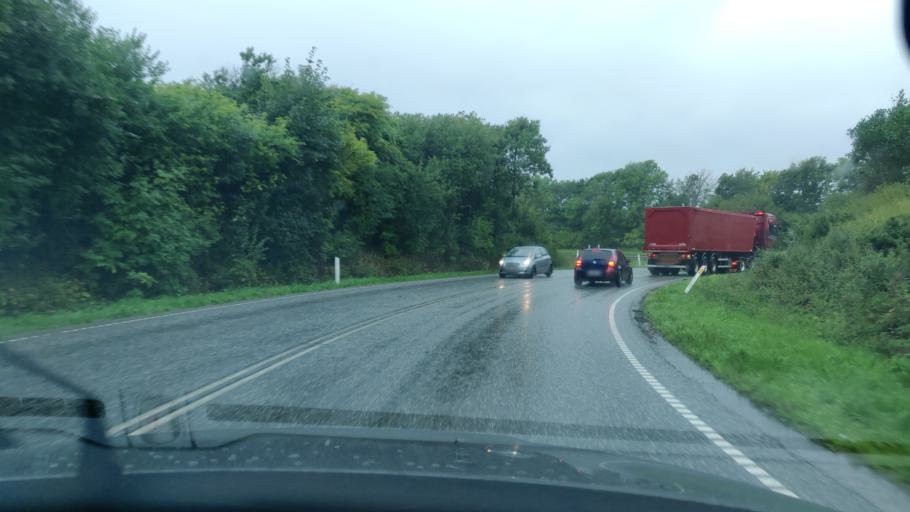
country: DK
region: North Denmark
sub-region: Thisted Kommune
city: Thisted
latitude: 56.8834
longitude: 8.5938
